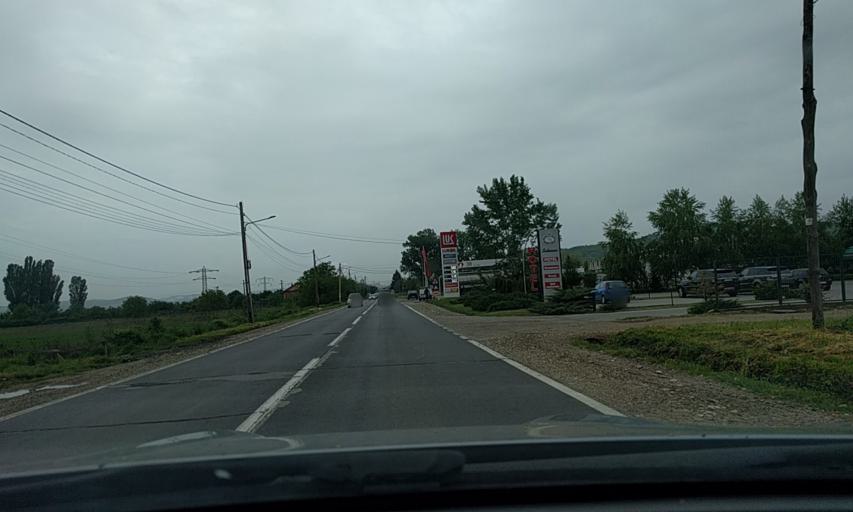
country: RO
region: Dambovita
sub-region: Comuna Aninoasa
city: Aninoasa
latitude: 44.9652
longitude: 25.4373
